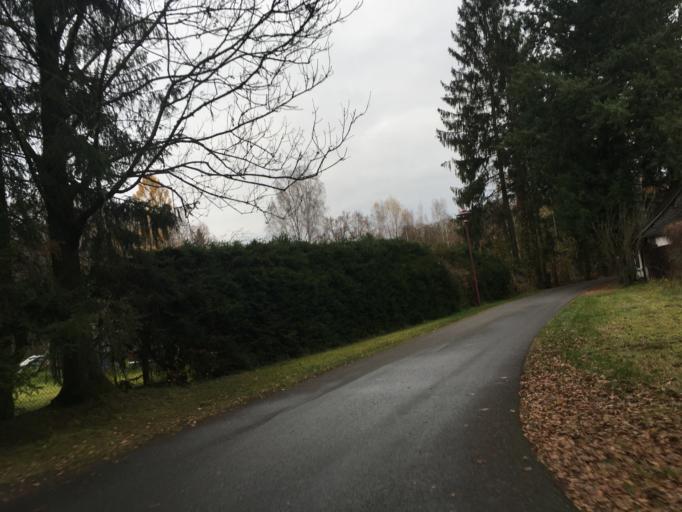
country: DE
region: Brandenburg
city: Mullrose
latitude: 52.2431
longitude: 14.4503
